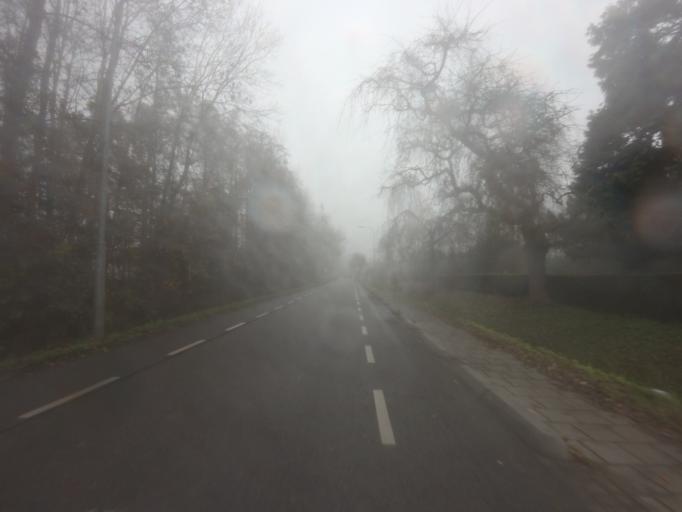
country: NL
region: Gelderland
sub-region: Gemeente Zaltbommel
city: Zaltbommel
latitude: 51.7981
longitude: 5.2067
